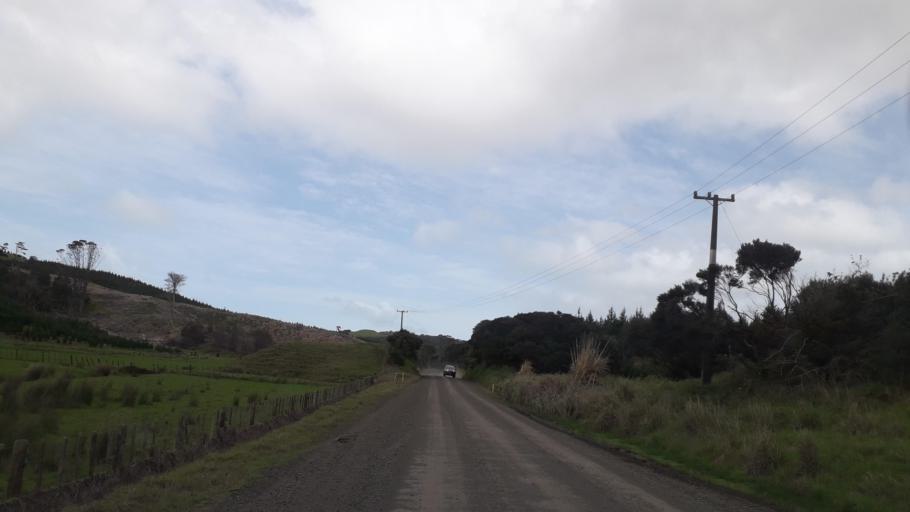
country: NZ
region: Northland
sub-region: Far North District
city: Ahipara
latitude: -35.4285
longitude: 173.3524
